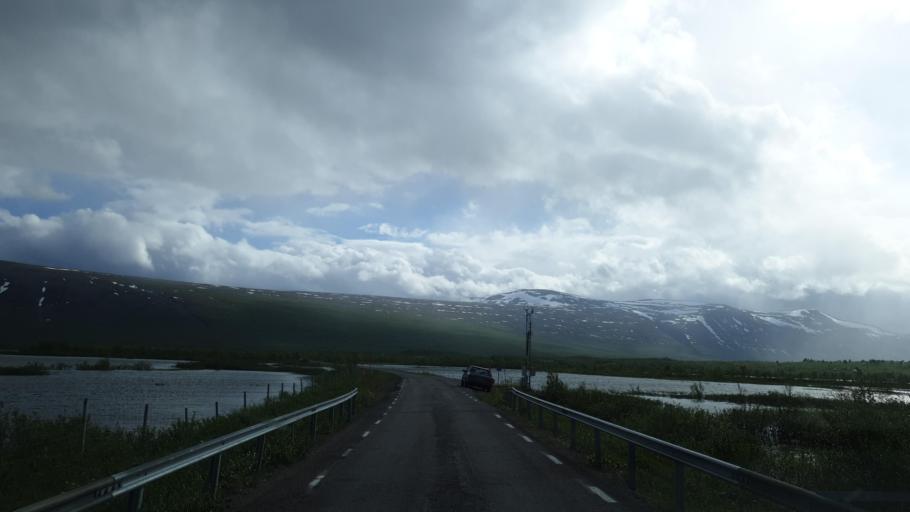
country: SE
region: Norrbotten
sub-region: Kiruna Kommun
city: Kiruna
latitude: 67.8605
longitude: 19.0284
